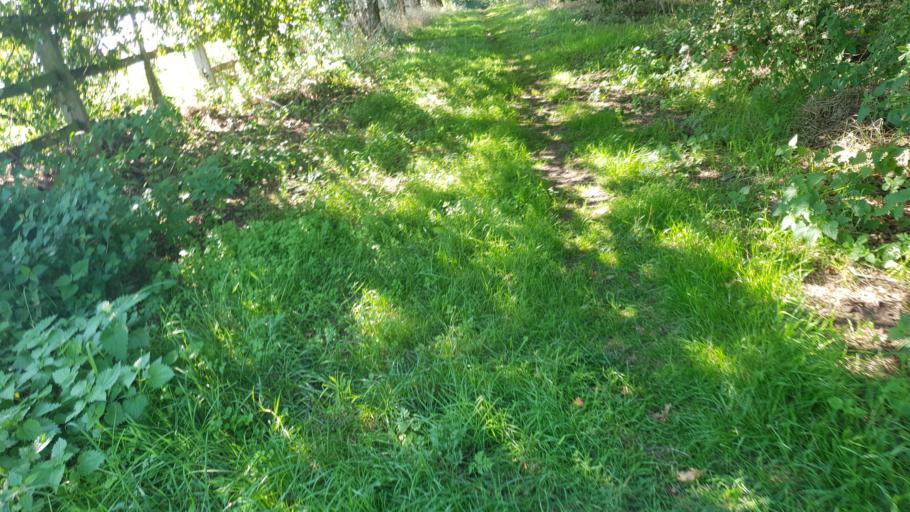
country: GB
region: England
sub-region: Essex
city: Wivenhoe
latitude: 51.9240
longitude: 0.9658
